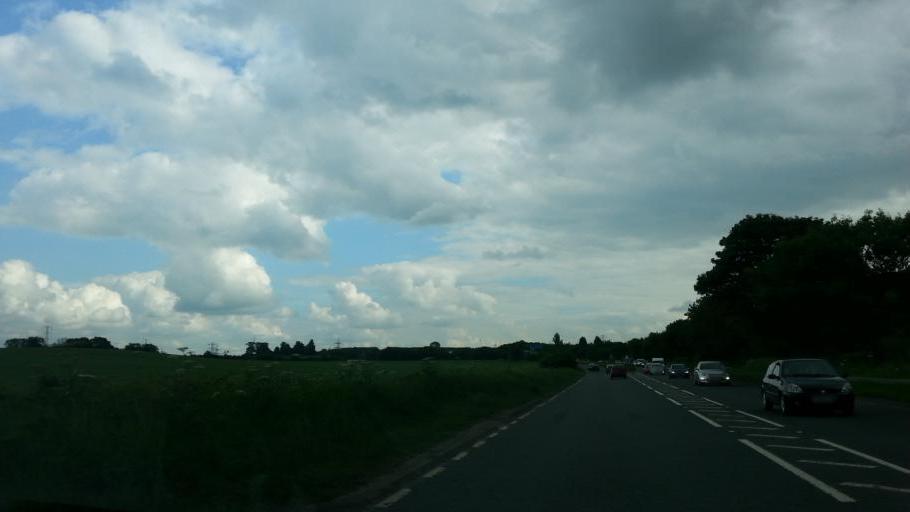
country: GB
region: England
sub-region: Warwickshire
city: Curdworth
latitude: 52.5480
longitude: -1.7292
